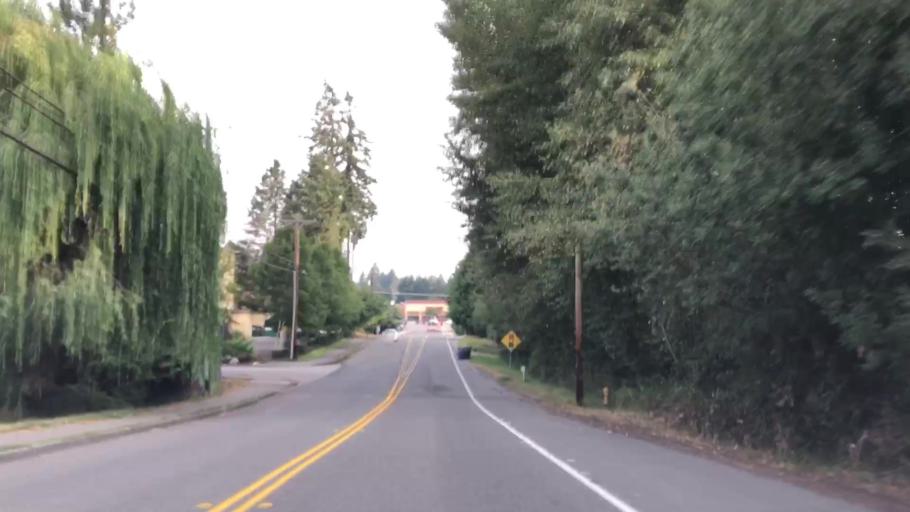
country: US
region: Washington
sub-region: King County
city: Bothell
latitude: 47.7891
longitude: -122.2130
